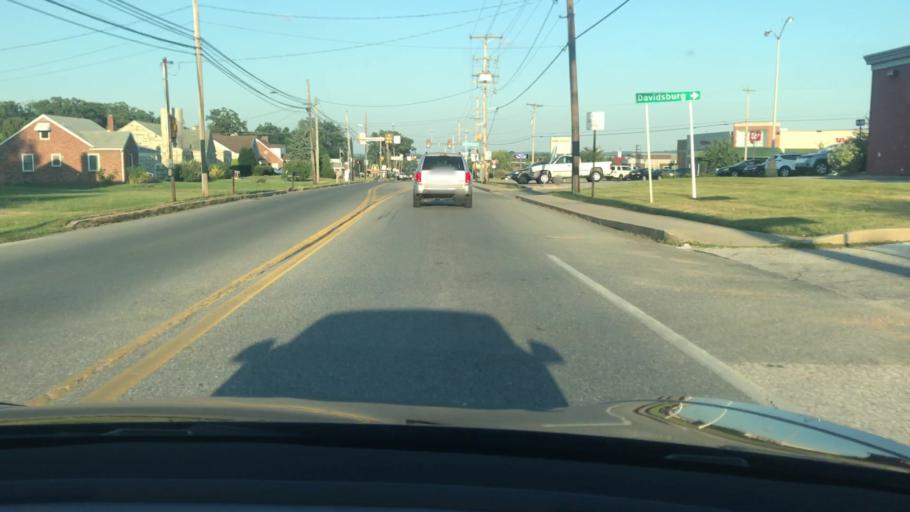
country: US
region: Pennsylvania
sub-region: York County
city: Weigelstown
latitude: 39.9843
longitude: -76.8254
